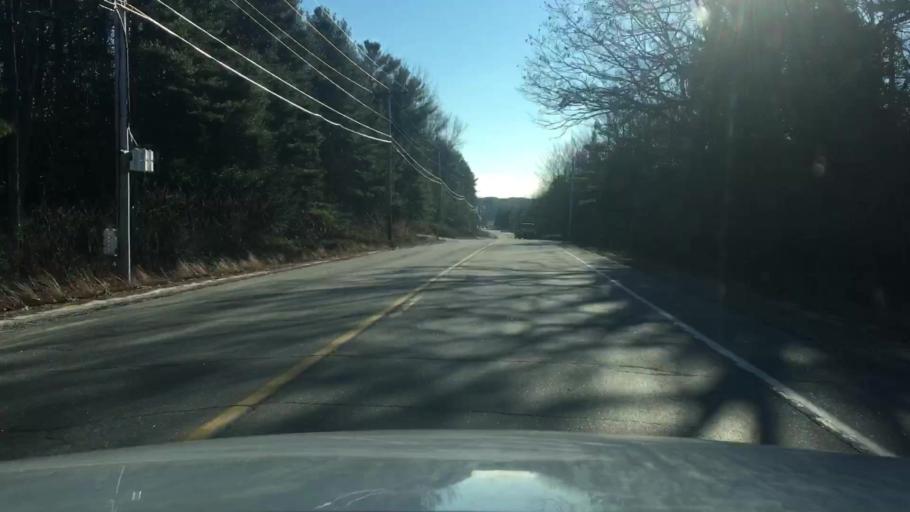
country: US
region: Maine
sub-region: Cumberland County
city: Brunswick
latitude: 43.8795
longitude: -69.9109
